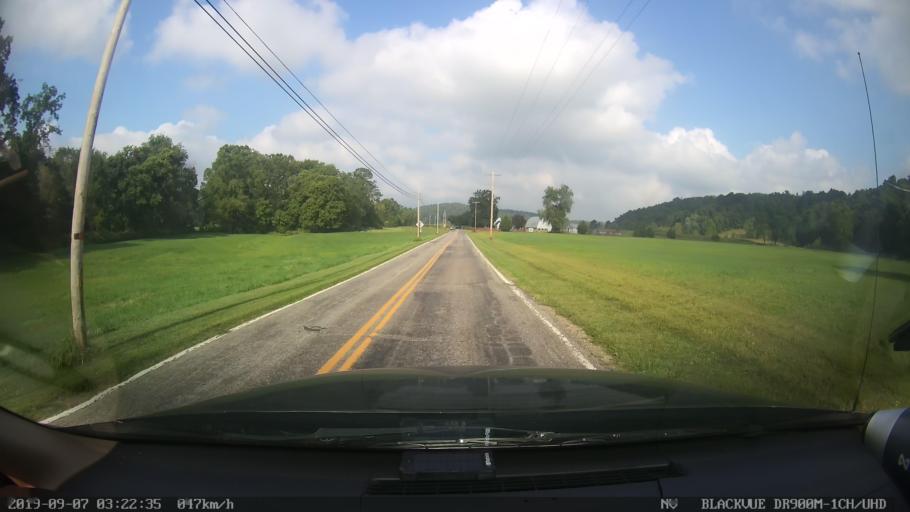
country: US
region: Ohio
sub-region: Licking County
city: Granville
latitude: 40.1181
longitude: -82.4612
